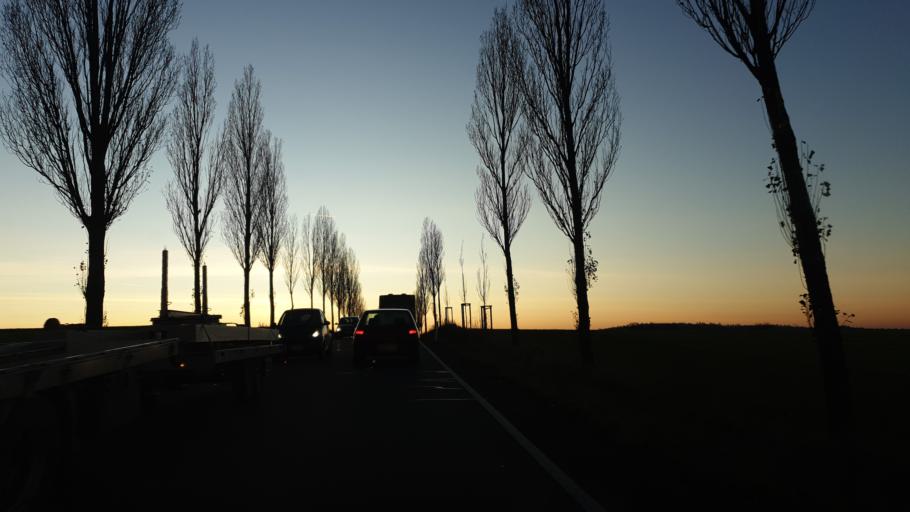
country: DE
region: Saxony
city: Hohndorf
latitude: 50.7503
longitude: 12.6774
